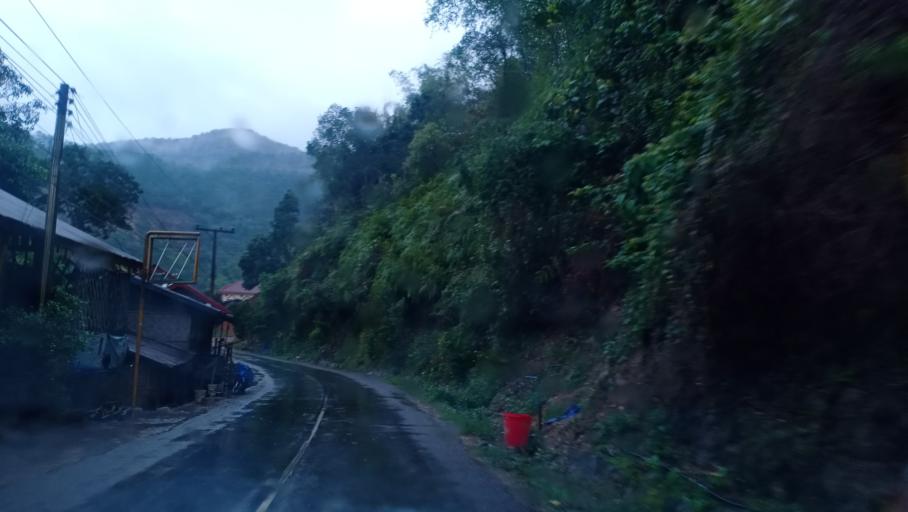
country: LA
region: Phongsali
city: Khoa
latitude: 21.0762
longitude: 102.5010
